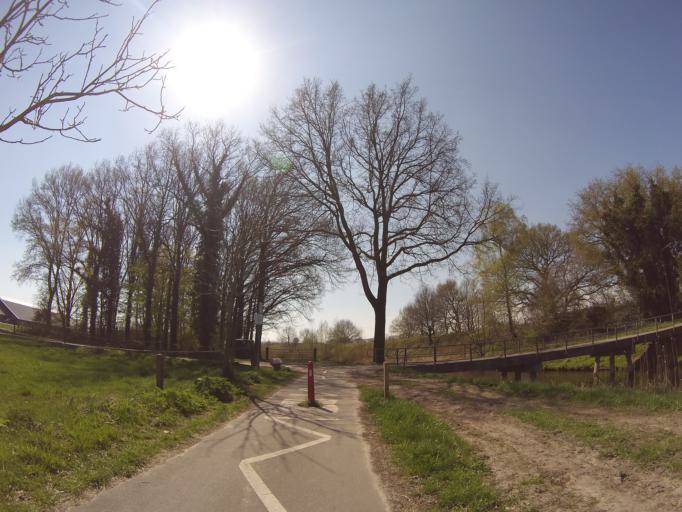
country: NL
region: Utrecht
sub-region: Gemeente Utrechtse Heuvelrug
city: Overberg
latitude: 52.0672
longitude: 5.4767
